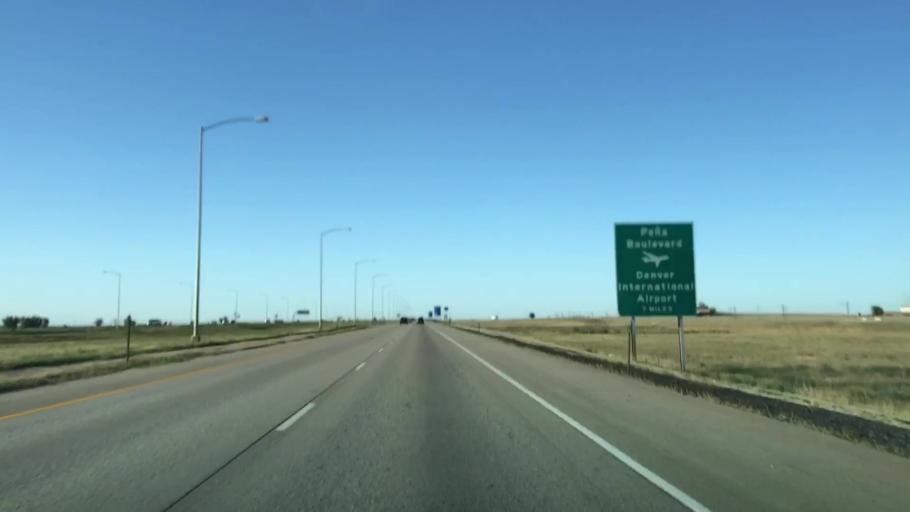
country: US
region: Colorado
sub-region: Adams County
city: Aurora
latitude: 39.8097
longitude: -104.7858
